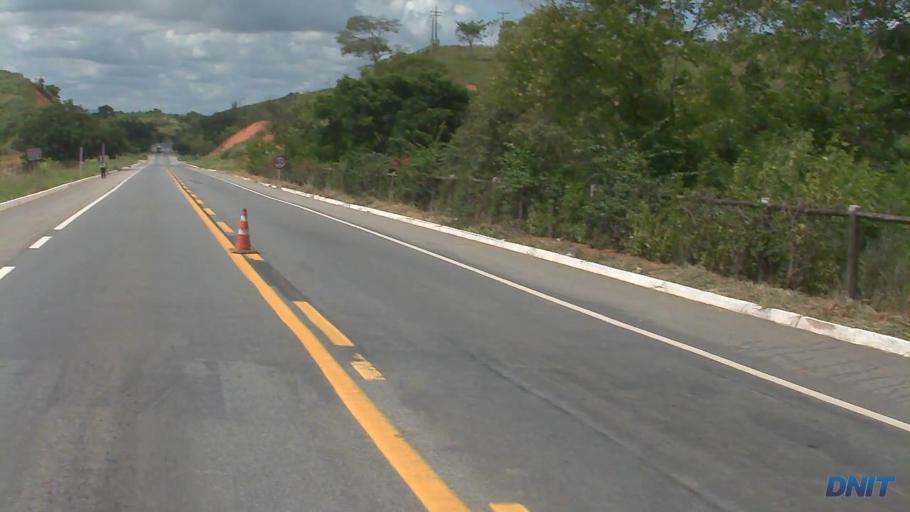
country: BR
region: Minas Gerais
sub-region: Governador Valadares
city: Governador Valadares
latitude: -18.9191
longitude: -42.0143
